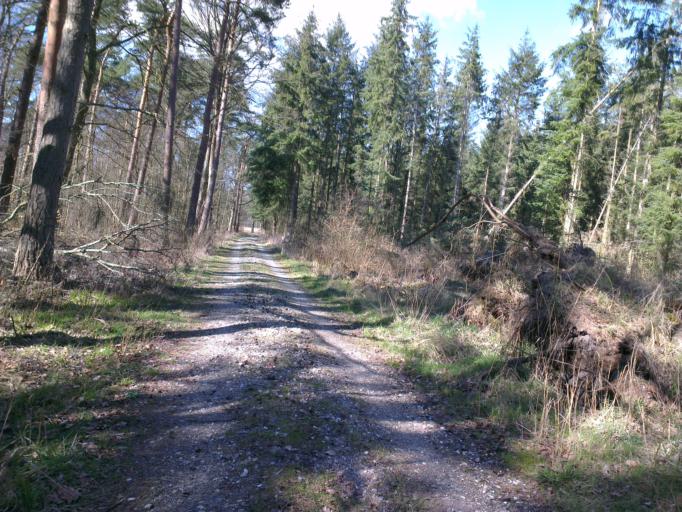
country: DK
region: Capital Region
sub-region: Frederikssund Kommune
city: Jaegerspris
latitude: 55.8849
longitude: 11.9971
